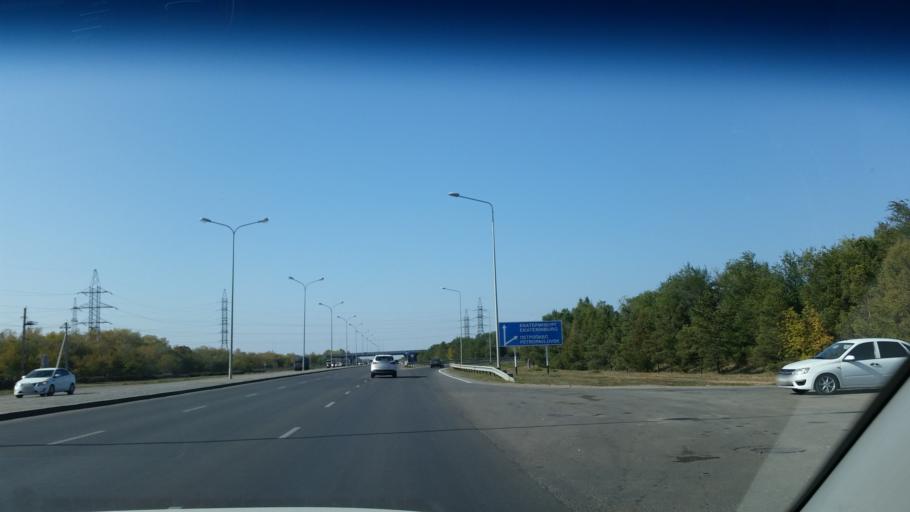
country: KZ
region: Astana Qalasy
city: Astana
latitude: 51.1979
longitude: 71.3131
